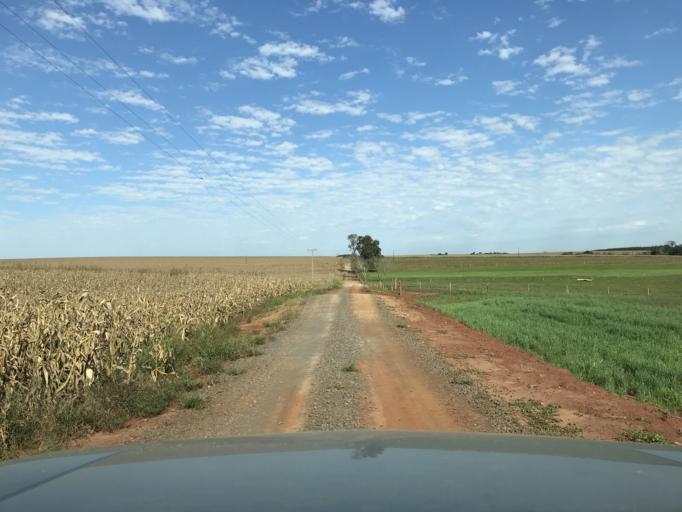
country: BR
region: Parana
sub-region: Palotina
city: Palotina
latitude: -24.1652
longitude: -53.7514
